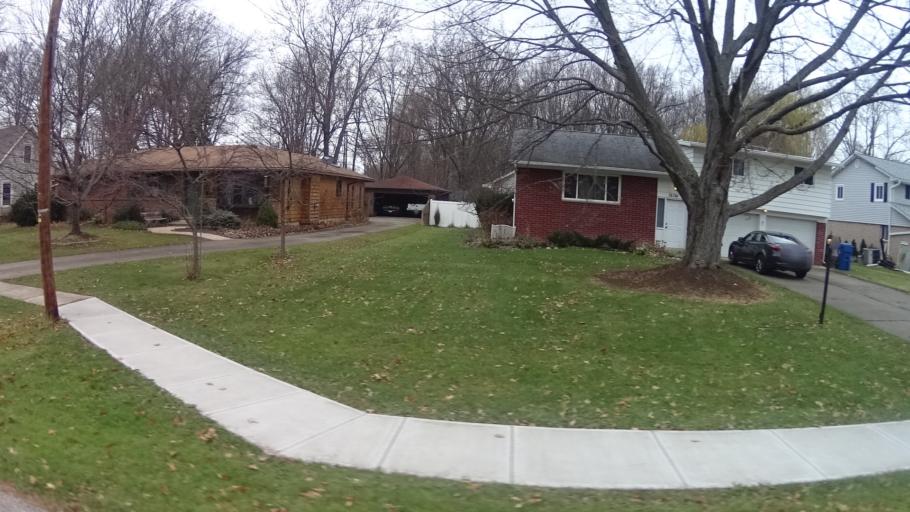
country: US
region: Ohio
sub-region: Lorain County
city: North Ridgeville
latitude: 41.3844
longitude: -82.0242
